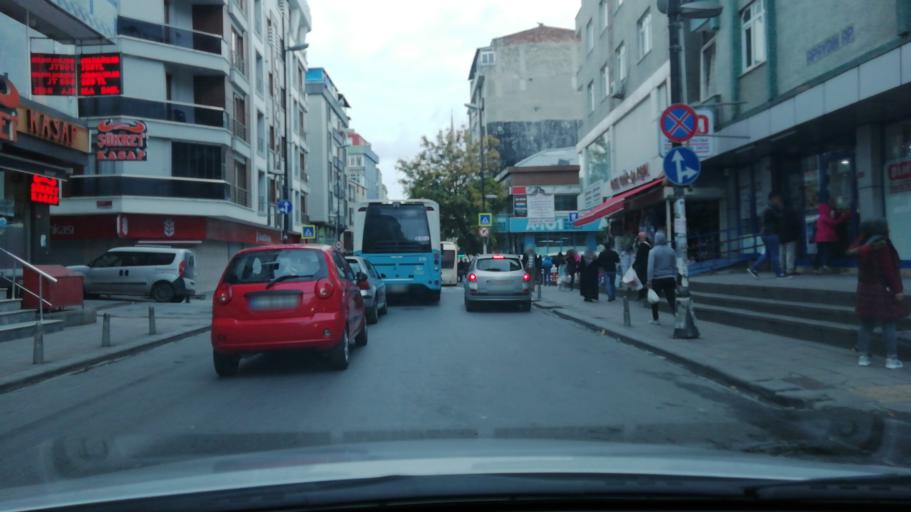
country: TR
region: Istanbul
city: Bahcelievler
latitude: 41.0058
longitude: 28.8387
